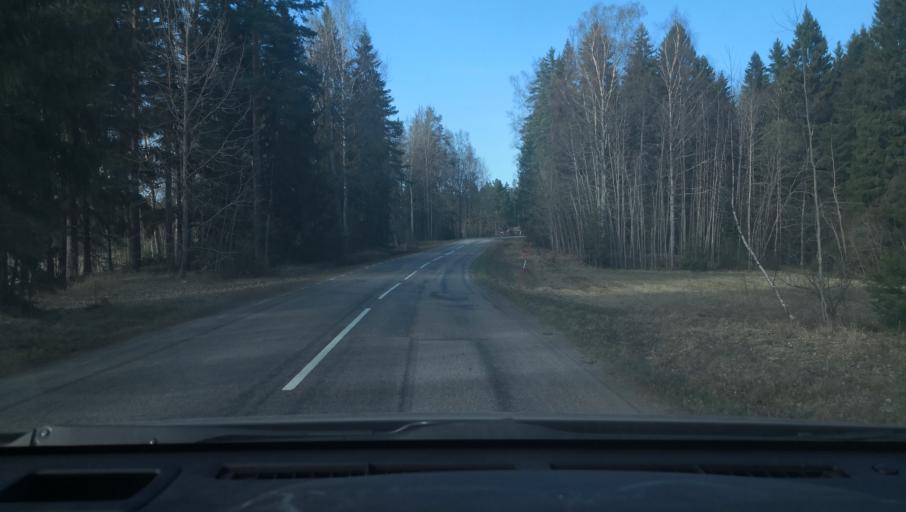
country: SE
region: Uppsala
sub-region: Heby Kommun
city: Heby
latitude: 59.9803
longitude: 16.9070
